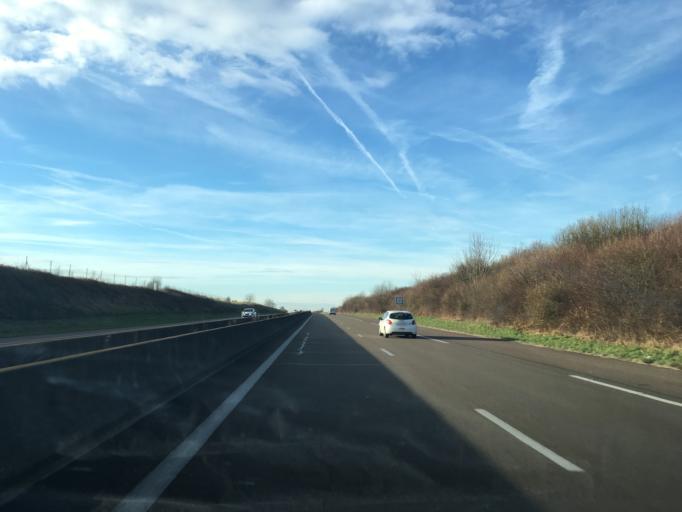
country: FR
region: Bourgogne
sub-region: Departement de l'Yonne
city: Avallon
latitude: 47.4993
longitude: 4.1107
